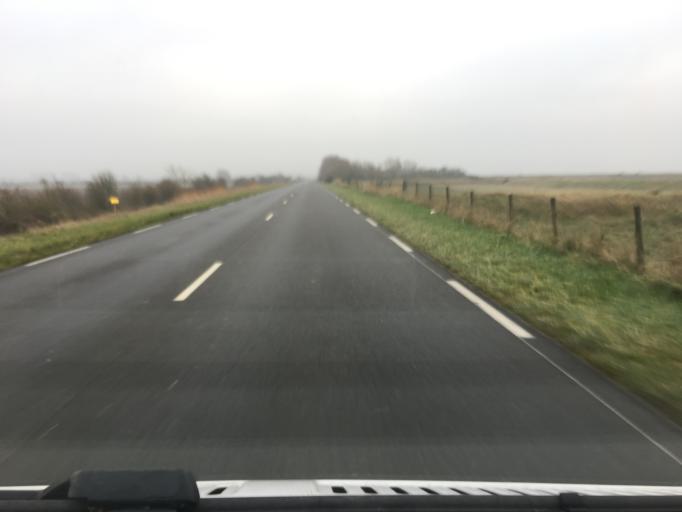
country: FR
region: Picardie
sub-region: Departement de la Somme
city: Le Crotoy
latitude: 50.2184
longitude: 1.6469
